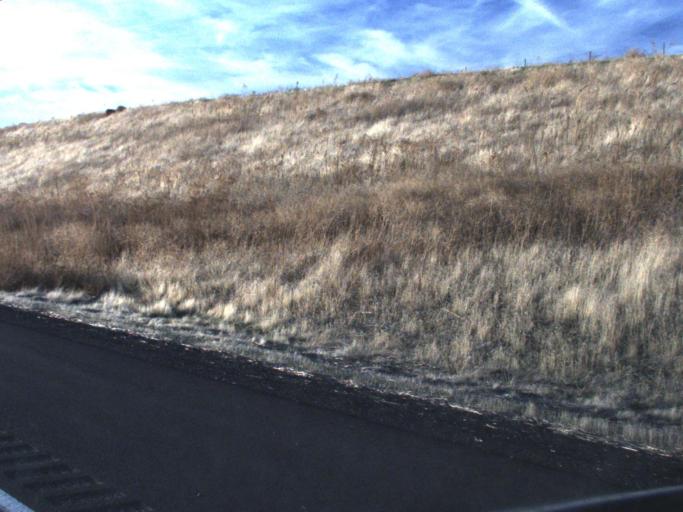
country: US
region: Washington
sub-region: Walla Walla County
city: Garrett
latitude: 46.0515
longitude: -118.5062
